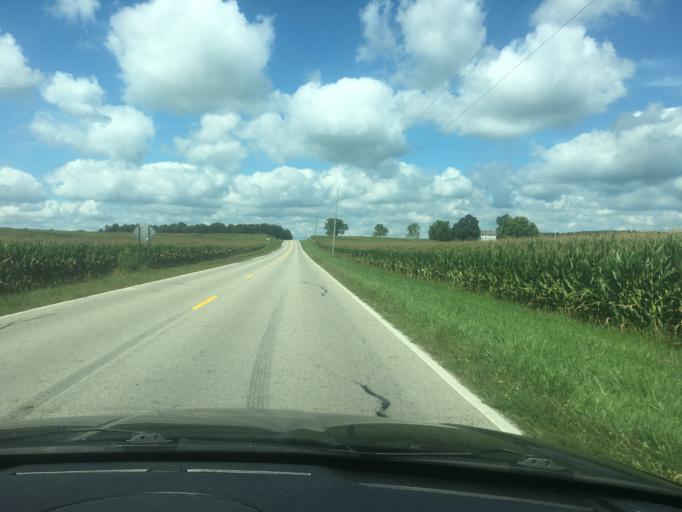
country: US
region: Ohio
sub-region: Logan County
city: West Liberty
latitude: 40.2308
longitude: -83.7084
